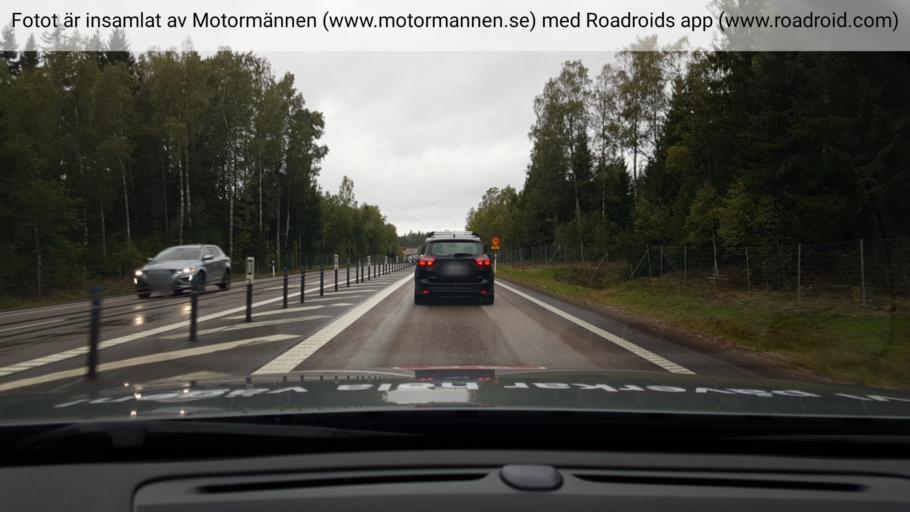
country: SE
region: Vaermland
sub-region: Kristinehamns Kommun
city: Kristinehamn
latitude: 59.3654
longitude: 14.0215
